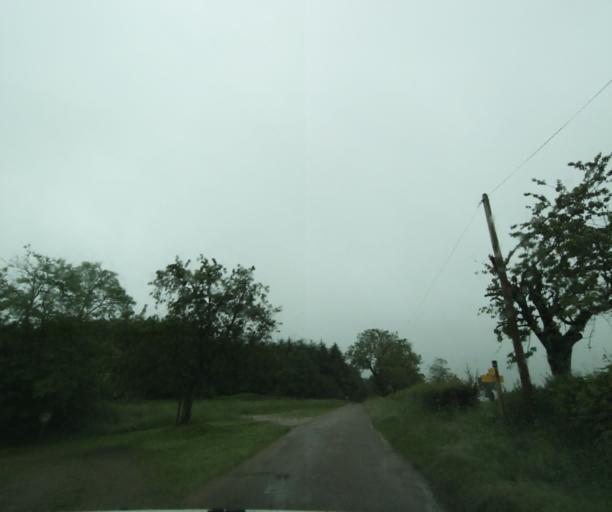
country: FR
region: Bourgogne
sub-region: Departement de Saone-et-Loire
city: Charolles
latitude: 46.3867
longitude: 4.3130
